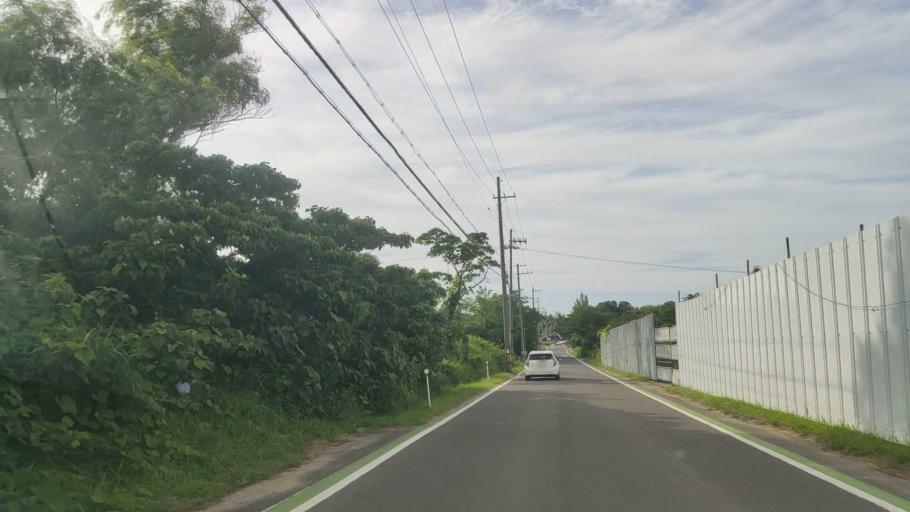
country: JP
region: Hyogo
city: Toyooka
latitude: 35.6354
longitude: 134.9287
